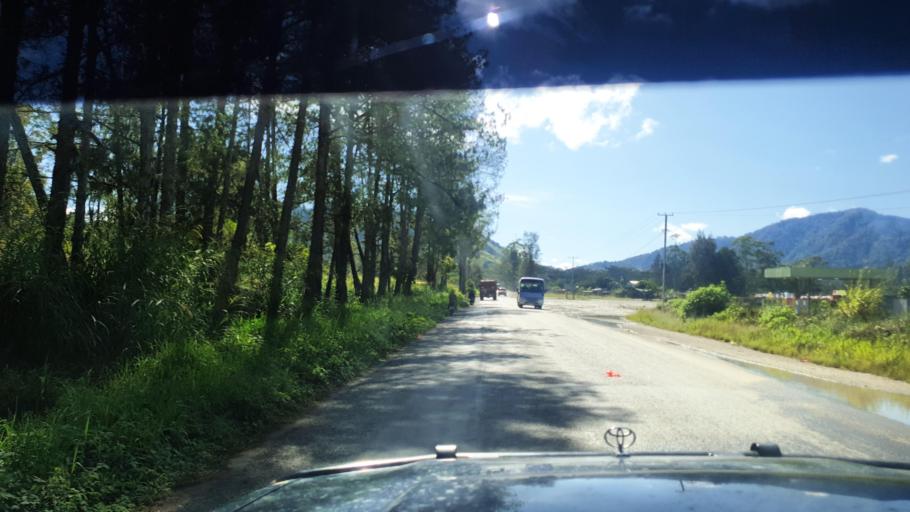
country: PG
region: Western Highlands
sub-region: Hagen
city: Mount Hagen
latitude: -5.8351
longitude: 144.3391
